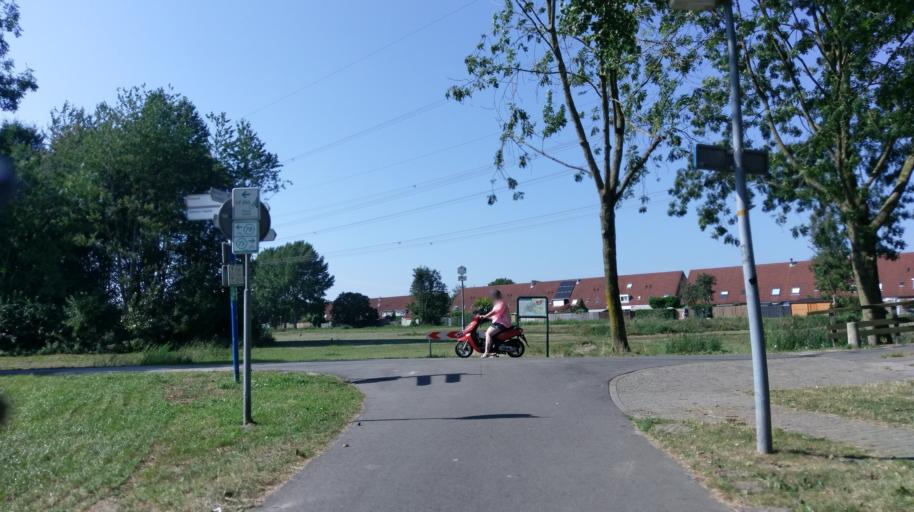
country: NL
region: Flevoland
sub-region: Gemeente Almere
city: Almere Stad
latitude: 52.3580
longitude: 5.2119
